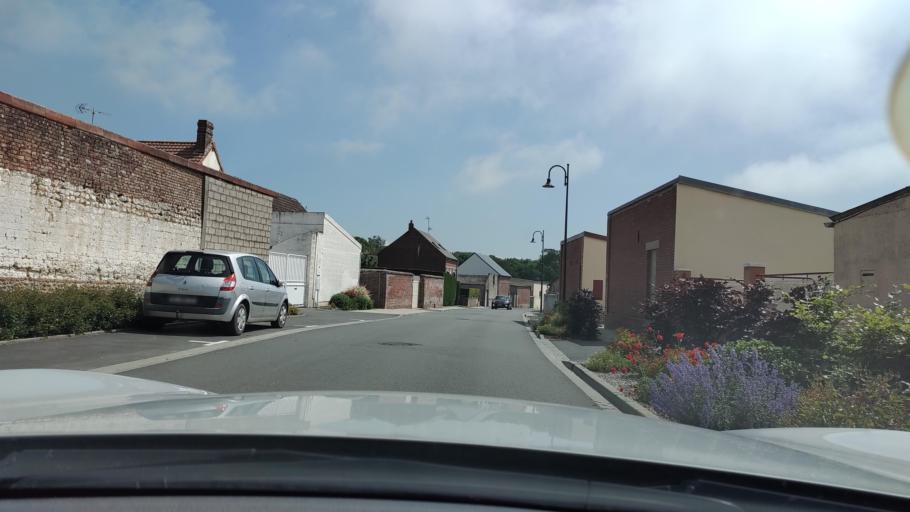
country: FR
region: Picardie
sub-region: Departement de la Somme
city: Ault
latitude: 50.0715
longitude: 1.4602
